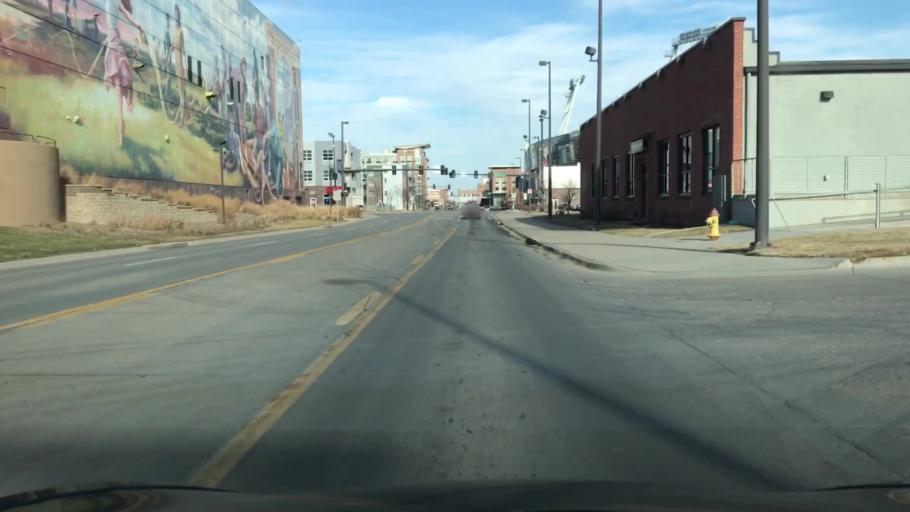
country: US
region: Nebraska
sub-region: Douglas County
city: Omaha
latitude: 41.2646
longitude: -95.9331
